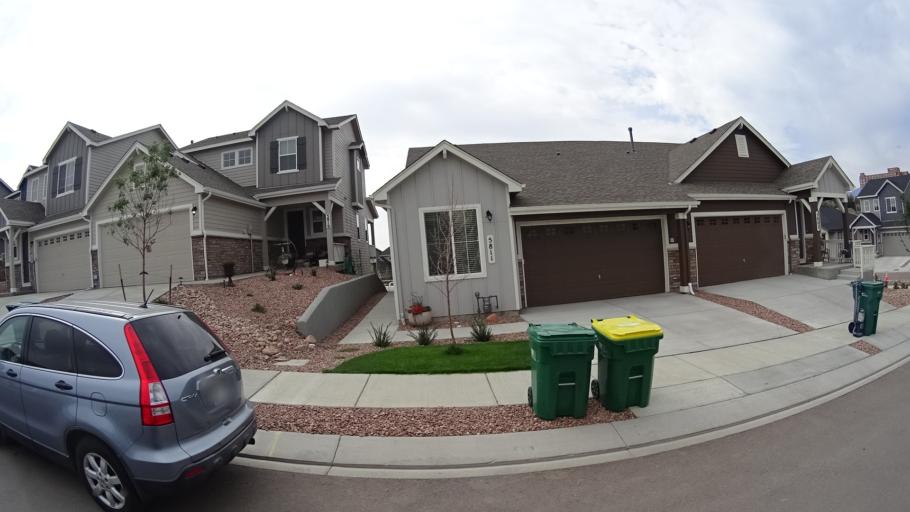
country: US
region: Colorado
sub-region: El Paso County
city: Colorado Springs
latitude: 38.9170
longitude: -104.8254
